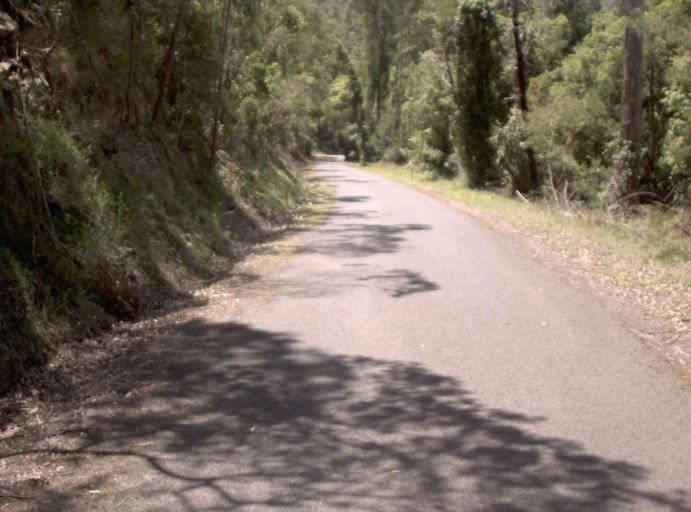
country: AU
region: New South Wales
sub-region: Bombala
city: Bombala
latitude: -37.4486
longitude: 148.9350
